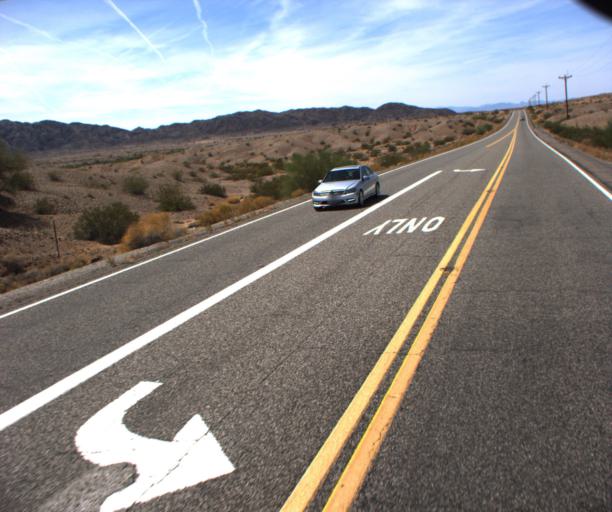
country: US
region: Arizona
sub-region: La Paz County
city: Parker
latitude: 34.0028
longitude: -114.2331
